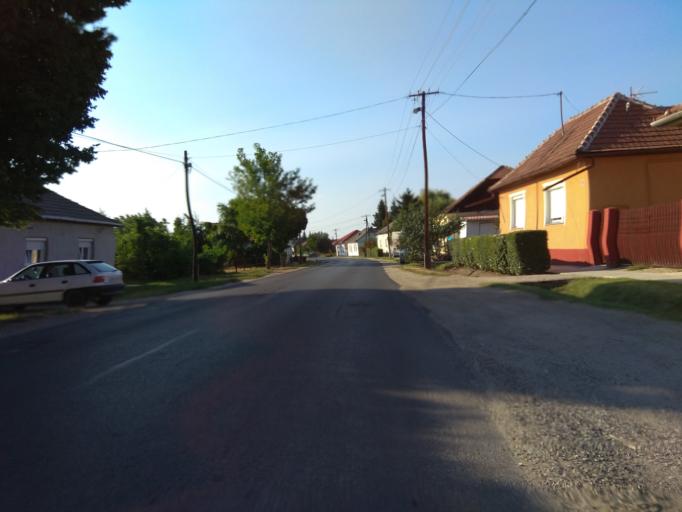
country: HU
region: Borsod-Abauj-Zemplen
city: Onod
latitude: 48.0041
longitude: 20.9170
